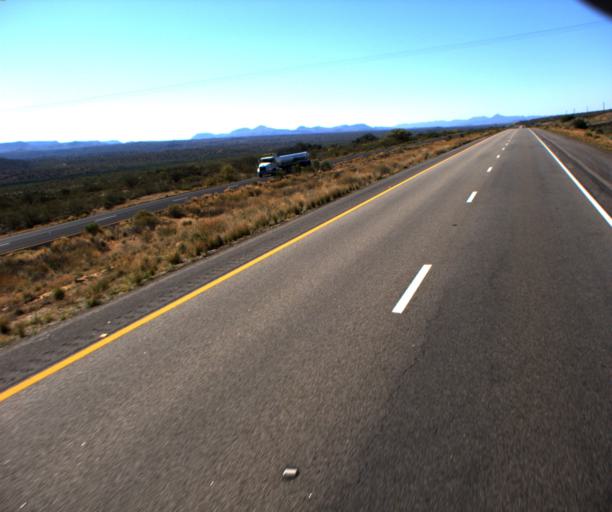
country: US
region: Arizona
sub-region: Mohave County
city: Kingman
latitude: 34.8531
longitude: -113.6389
